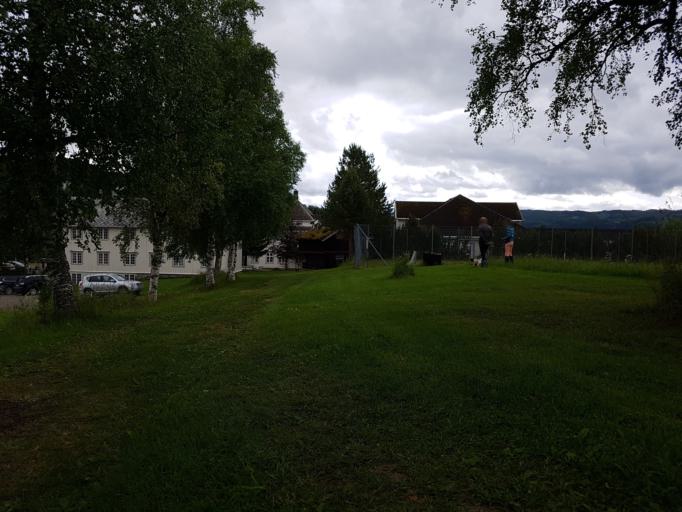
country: NO
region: Sor-Trondelag
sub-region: Selbu
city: Mebonden
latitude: 63.2335
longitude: 11.0291
